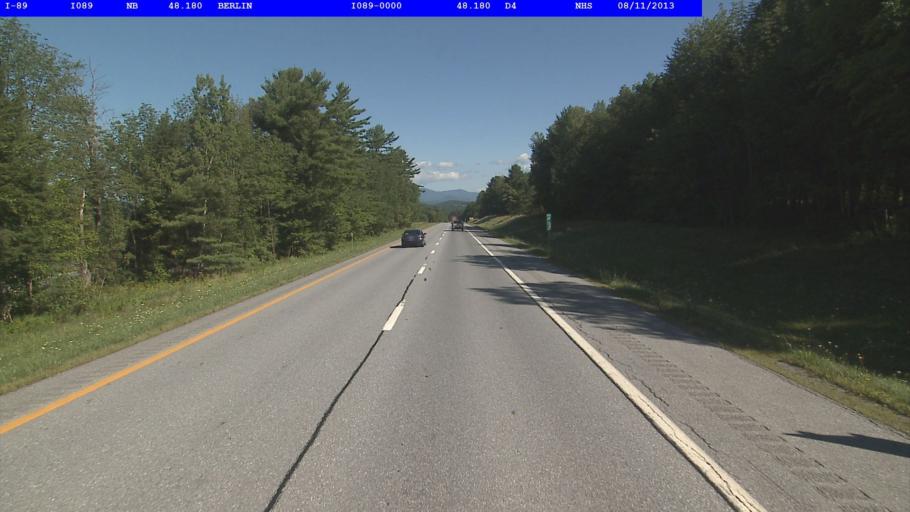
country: US
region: Vermont
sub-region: Washington County
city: South Barre
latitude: 44.1858
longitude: -72.5759
